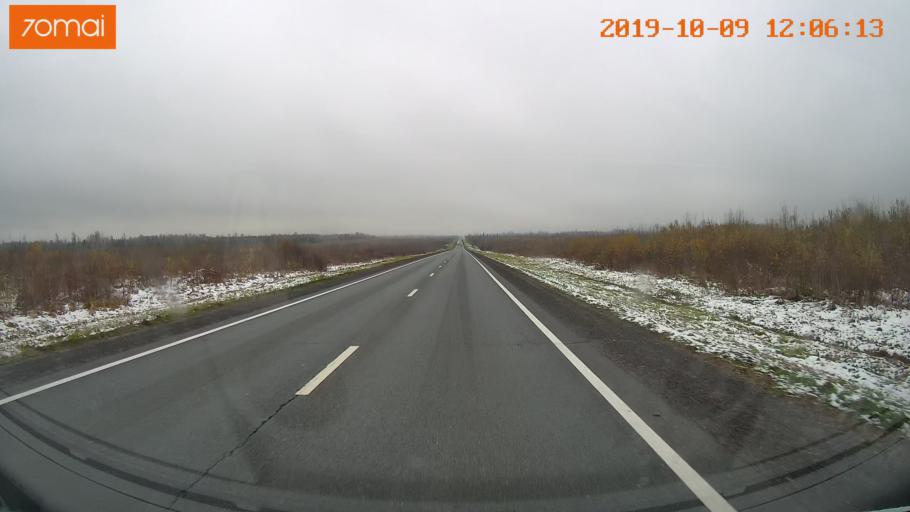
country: RU
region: Jaroslavl
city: Prechistoye
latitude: 58.6178
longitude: 40.3337
